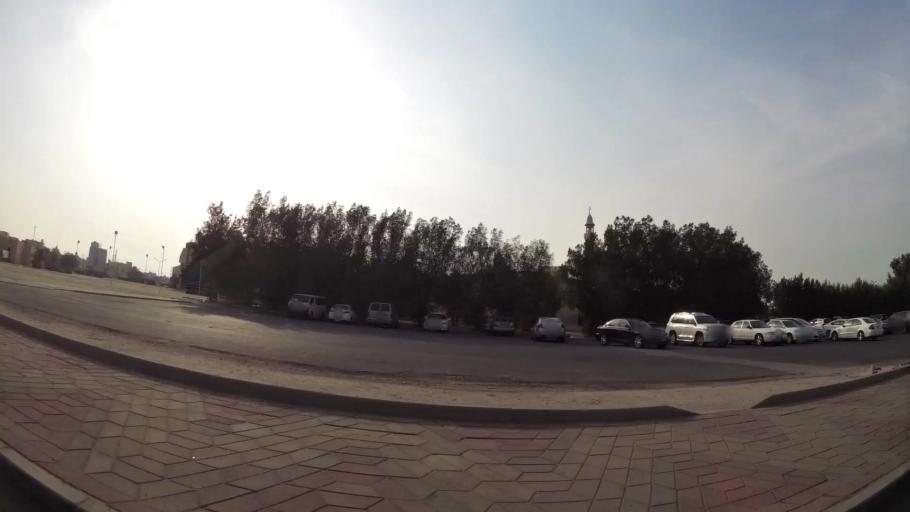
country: KW
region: Mubarak al Kabir
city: Sabah as Salim
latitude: 29.2560
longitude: 48.0543
